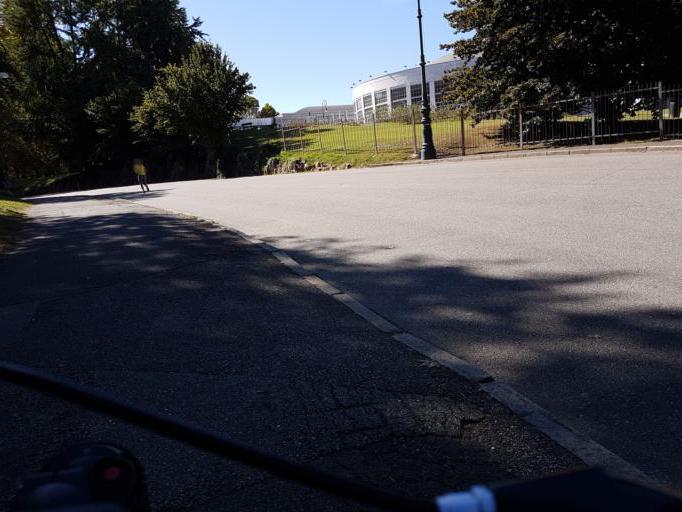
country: IT
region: Piedmont
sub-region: Provincia di Torino
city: Turin
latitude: 45.0491
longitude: 7.6844
